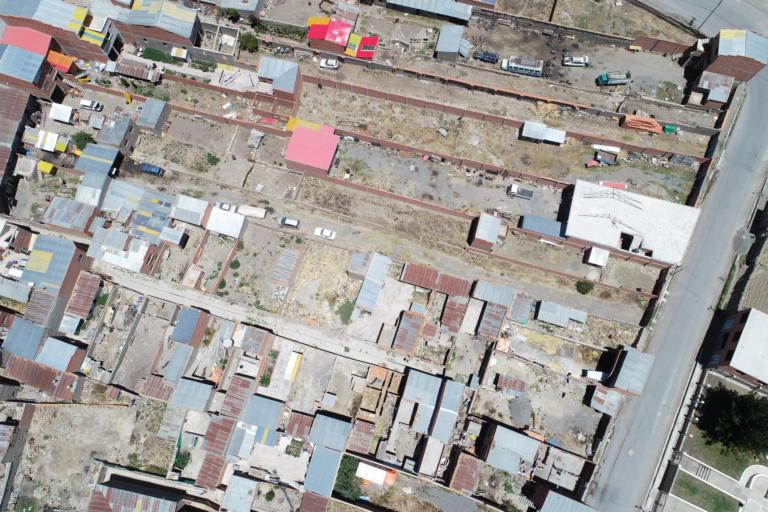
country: BO
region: La Paz
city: Achacachi
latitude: -16.0399
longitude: -68.6852
